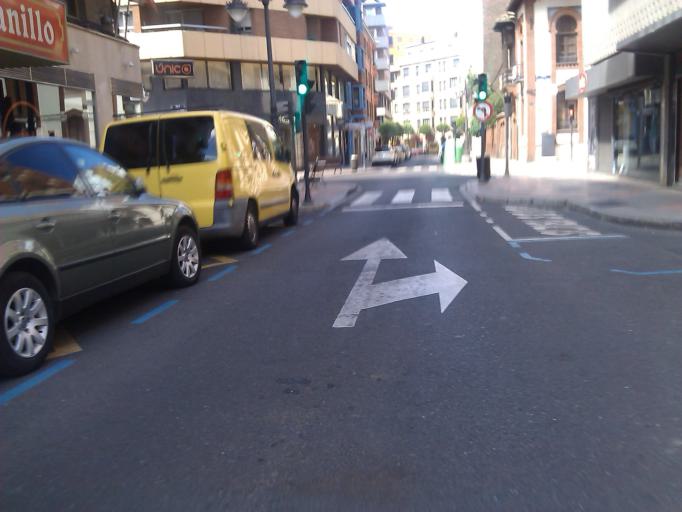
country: ES
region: Castille and Leon
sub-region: Provincia de Leon
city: Leon
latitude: 42.5984
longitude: -5.5754
